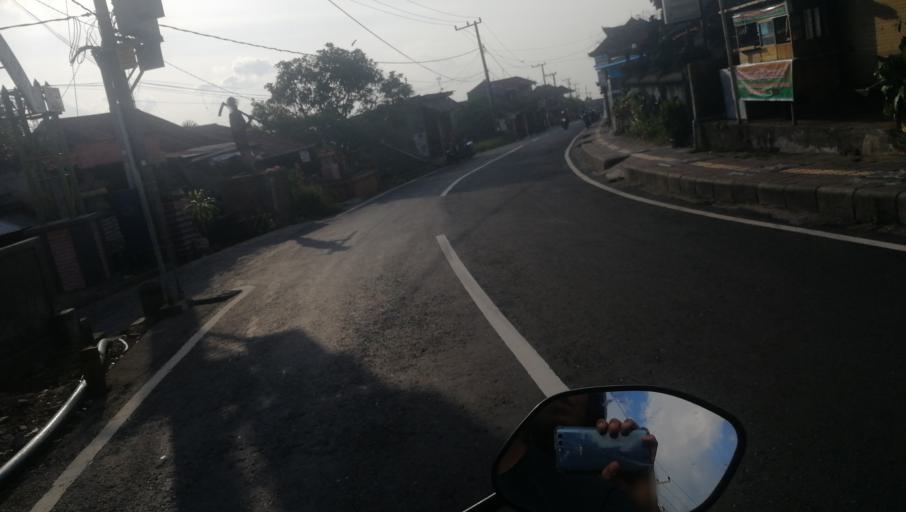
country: ID
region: Bali
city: Munduk
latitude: -8.2665
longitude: 115.0545
